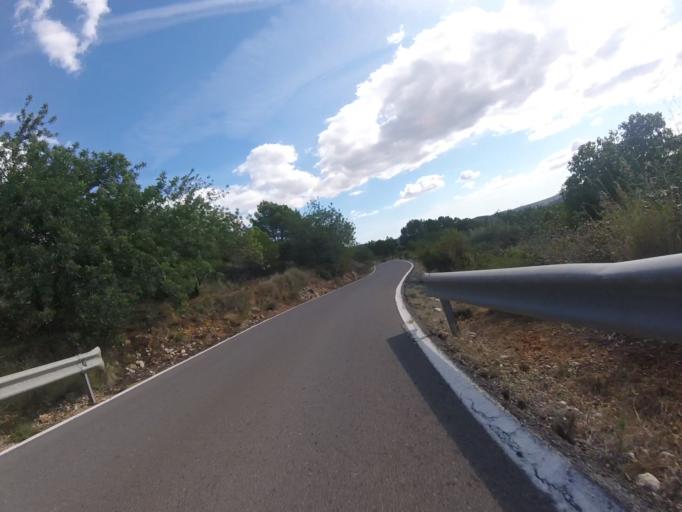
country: ES
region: Valencia
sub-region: Provincia de Castello
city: Cuevas de Vinroma
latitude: 40.3753
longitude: 0.1143
